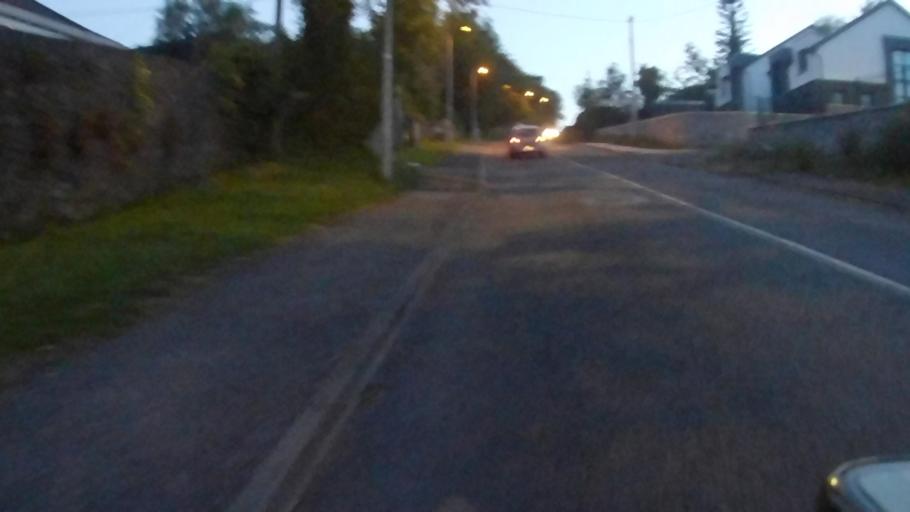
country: IE
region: Munster
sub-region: County Cork
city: Passage West
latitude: 51.9267
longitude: -8.3993
